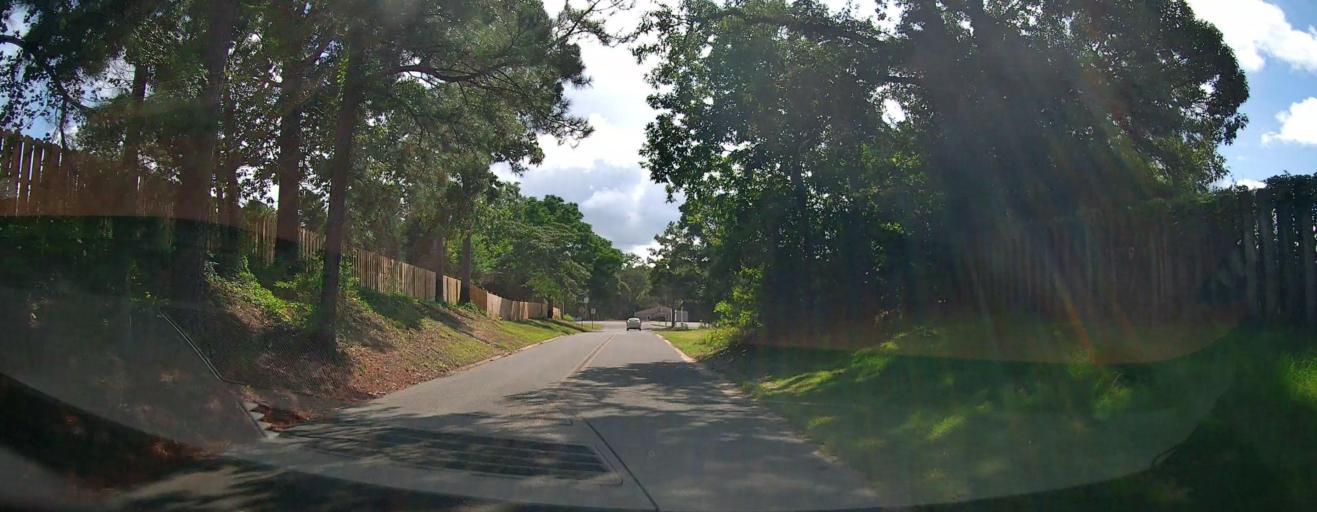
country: US
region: Georgia
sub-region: Houston County
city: Warner Robins
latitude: 32.5851
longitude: -83.6246
